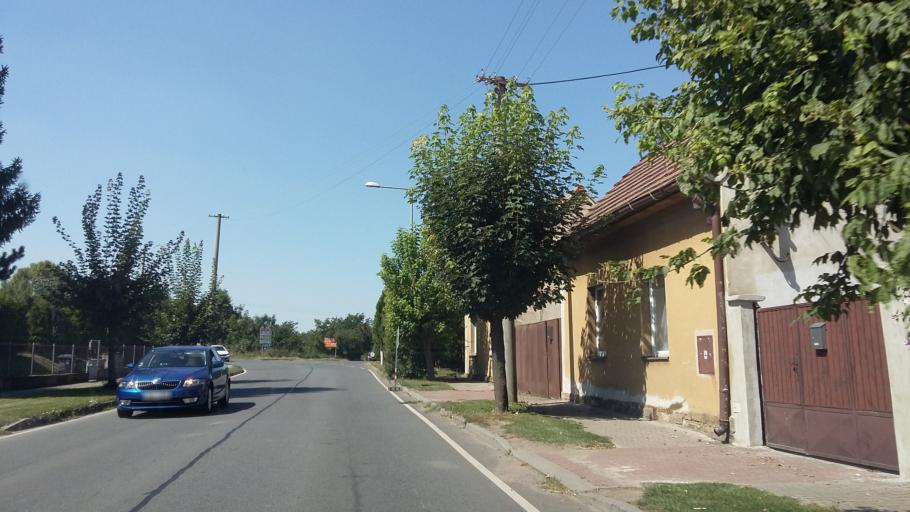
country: CZ
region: Central Bohemia
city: Brandys nad Labem-Stara Boleslav
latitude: 50.1656
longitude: 14.6771
